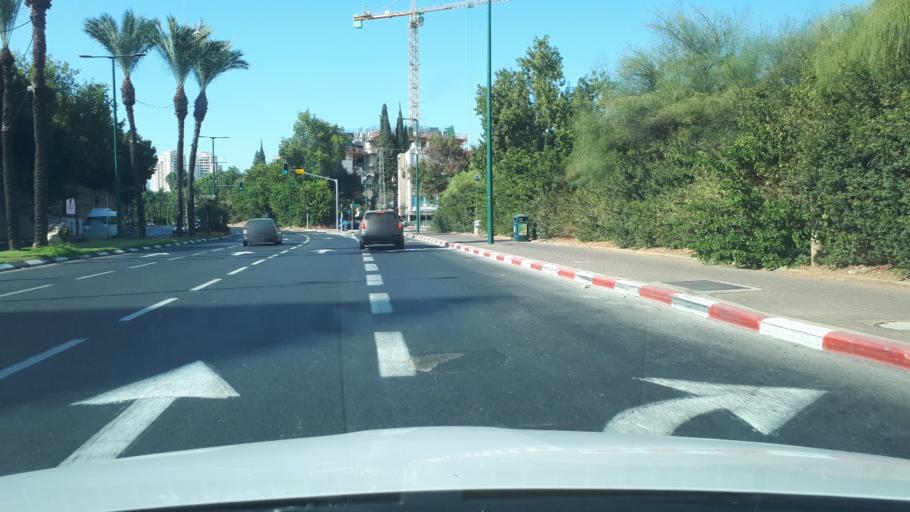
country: IL
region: Tel Aviv
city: Giv`atayim
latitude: 32.0606
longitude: 34.8210
